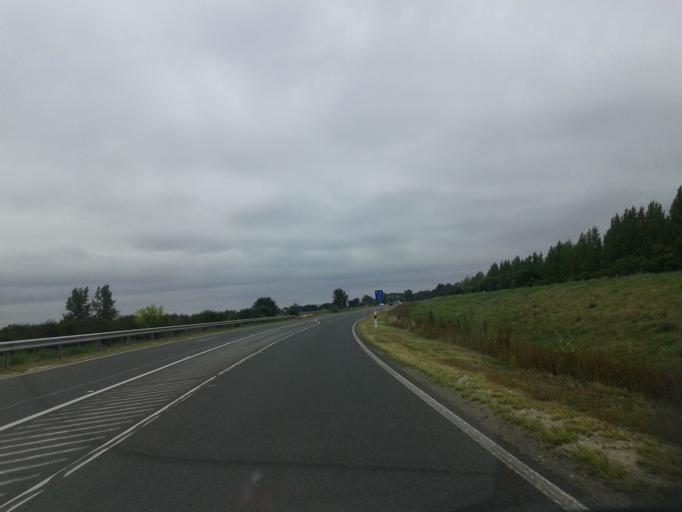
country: HU
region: Bacs-Kiskun
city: Harta
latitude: 46.7316
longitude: 19.0153
